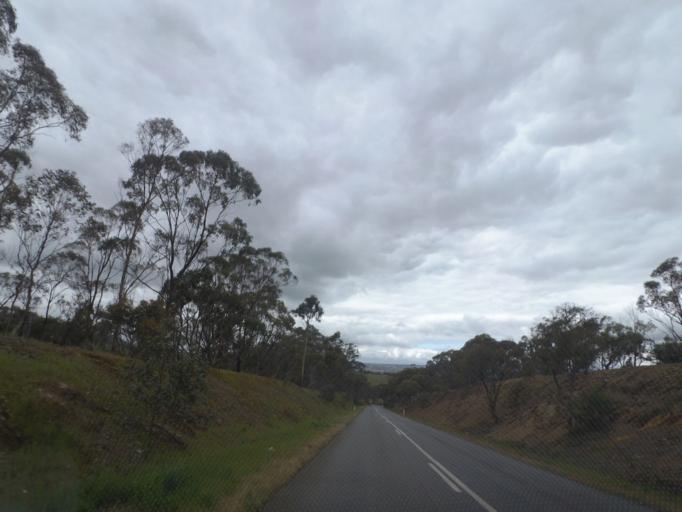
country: AU
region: Victoria
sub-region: Hume
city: Sunbury
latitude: -37.3974
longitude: 144.8408
